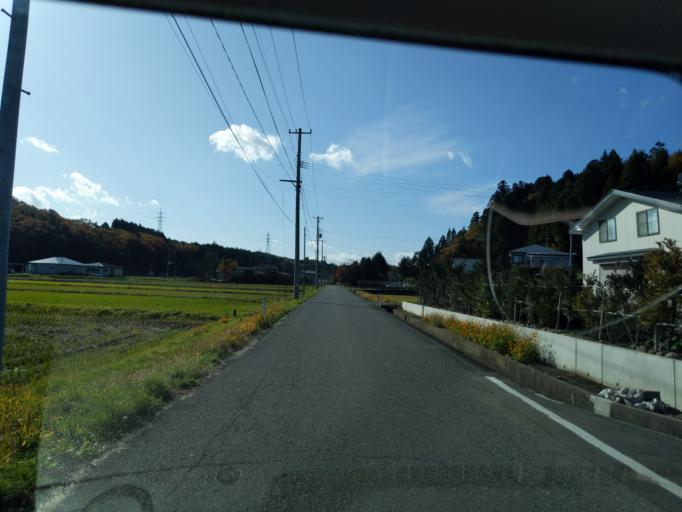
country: JP
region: Iwate
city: Mizusawa
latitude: 39.0941
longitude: 141.1321
